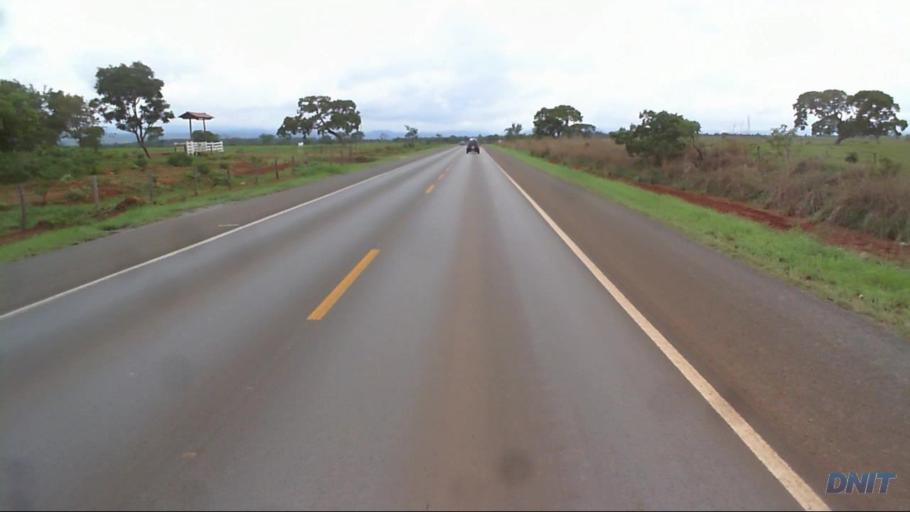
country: BR
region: Goias
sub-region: Padre Bernardo
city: Padre Bernardo
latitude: -15.1606
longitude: -48.3591
